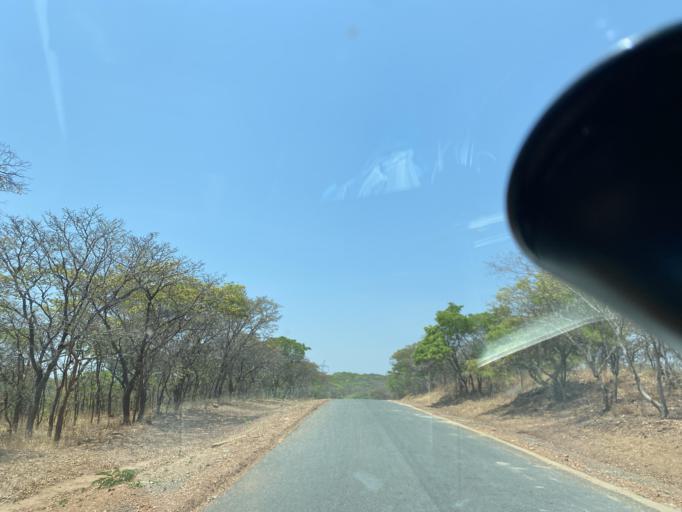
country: ZM
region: Lusaka
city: Kafue
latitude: -15.8501
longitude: 28.4164
